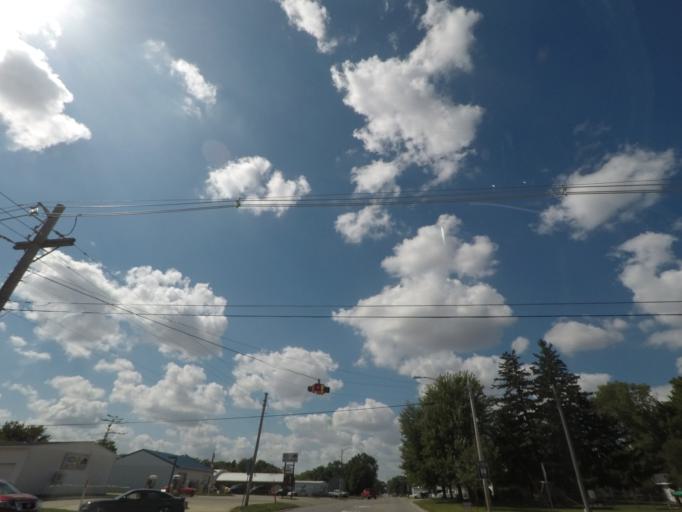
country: US
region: Iowa
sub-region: Story County
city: Nevada
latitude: 42.0228
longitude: -93.4398
